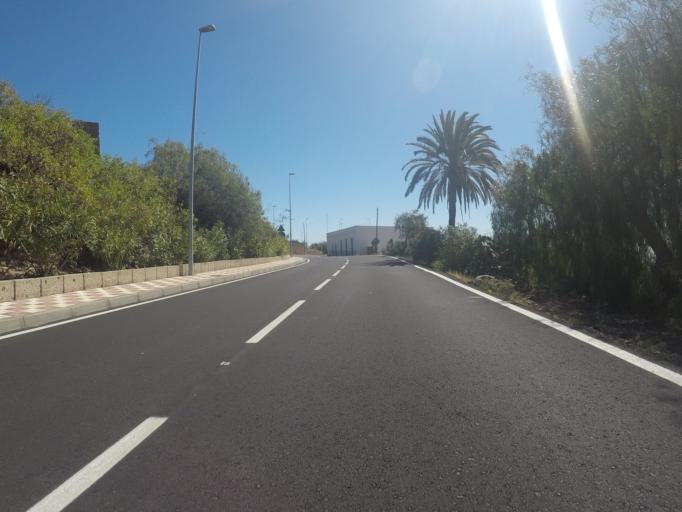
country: ES
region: Canary Islands
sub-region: Provincia de Santa Cruz de Tenerife
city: Lomo de Arico
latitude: 28.1800
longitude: -16.4818
